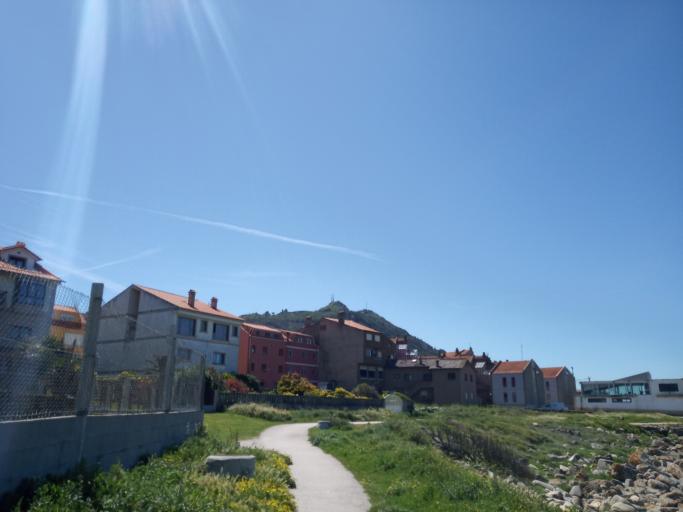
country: ES
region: Galicia
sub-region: Provincia de Pontevedra
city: A Guarda
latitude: 41.9045
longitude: -8.8794
